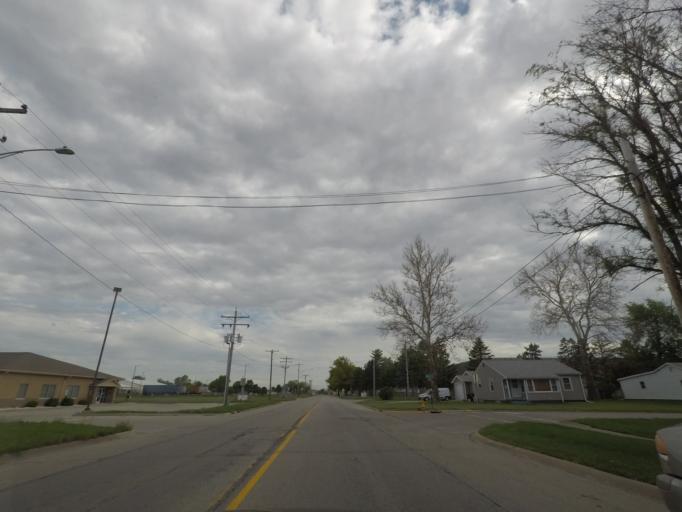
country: US
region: Illinois
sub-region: Logan County
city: Lincoln
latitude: 40.1398
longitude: -89.3488
